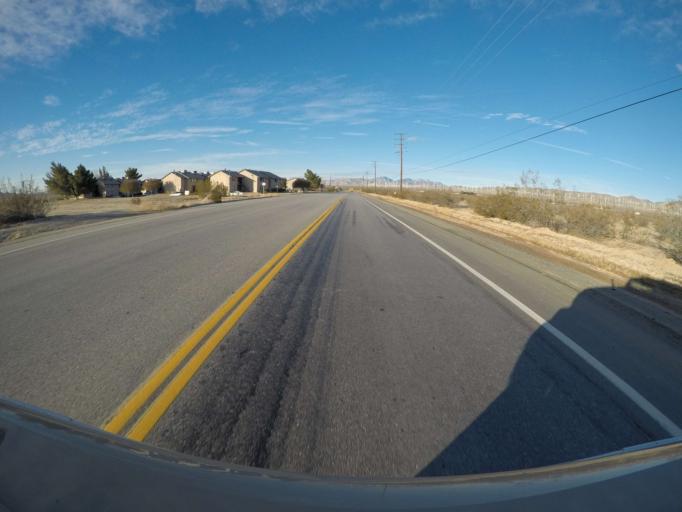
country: US
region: California
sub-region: Kern County
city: Mojave
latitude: 35.0568
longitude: -118.1812
